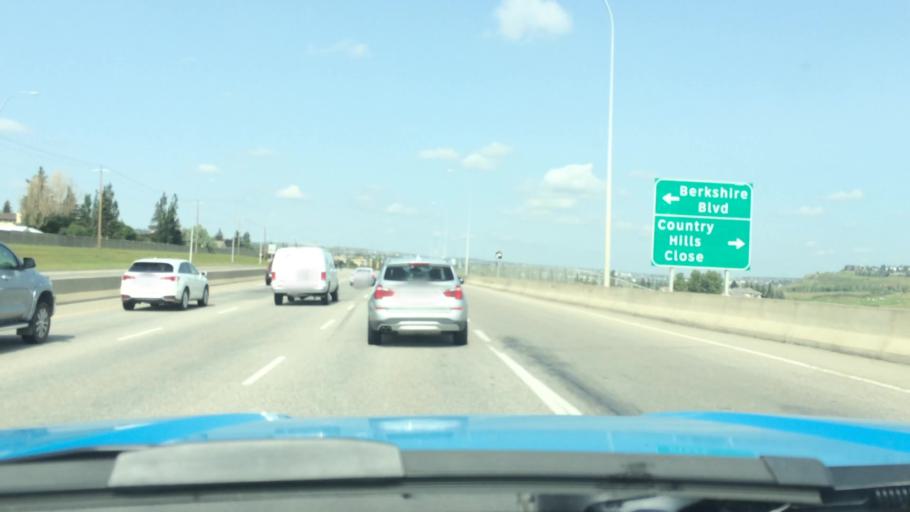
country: CA
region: Alberta
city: Calgary
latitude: 51.1372
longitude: -114.0763
